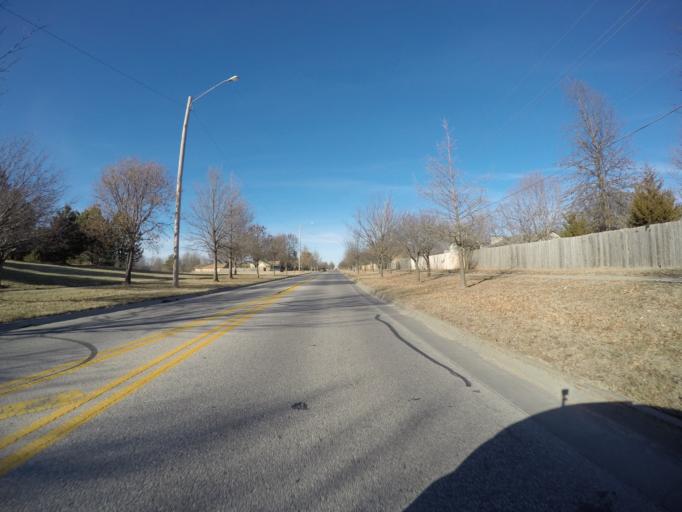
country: US
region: Kansas
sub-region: Sedgwick County
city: Maize
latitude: 37.7174
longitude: -97.4811
